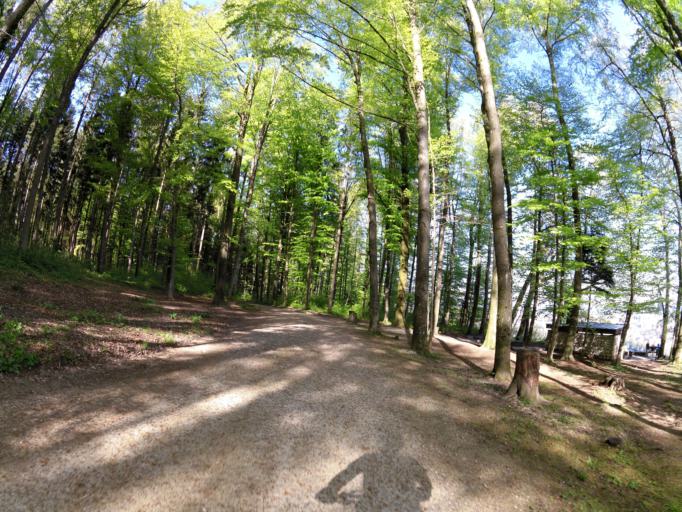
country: CH
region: Aargau
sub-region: Bezirk Aarau
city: Aarau
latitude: 47.3987
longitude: 8.0363
